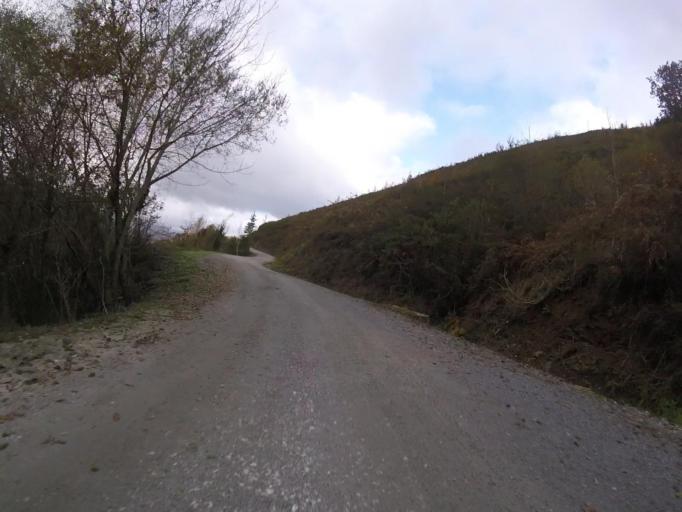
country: ES
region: Navarre
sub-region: Provincia de Navarra
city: Goizueta
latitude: 43.2100
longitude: -1.8529
